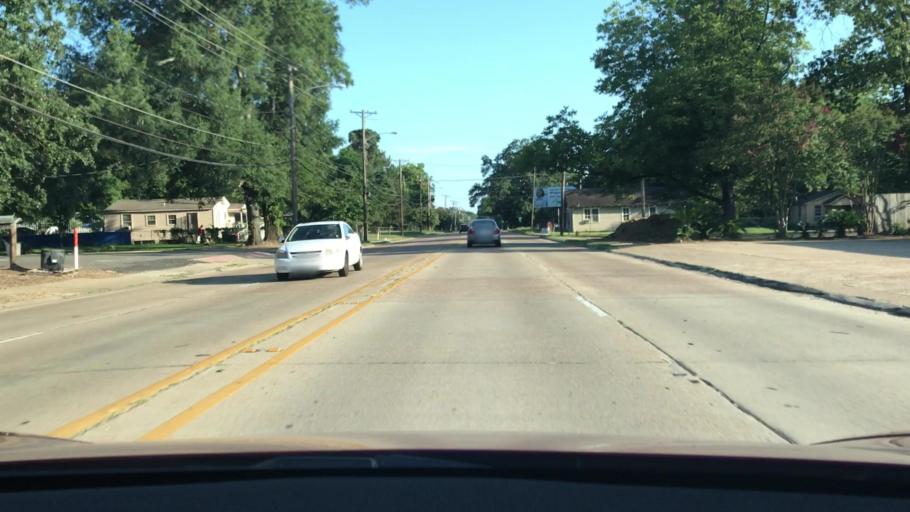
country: US
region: Louisiana
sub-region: Bossier Parish
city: Bossier City
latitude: 32.4404
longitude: -93.7460
